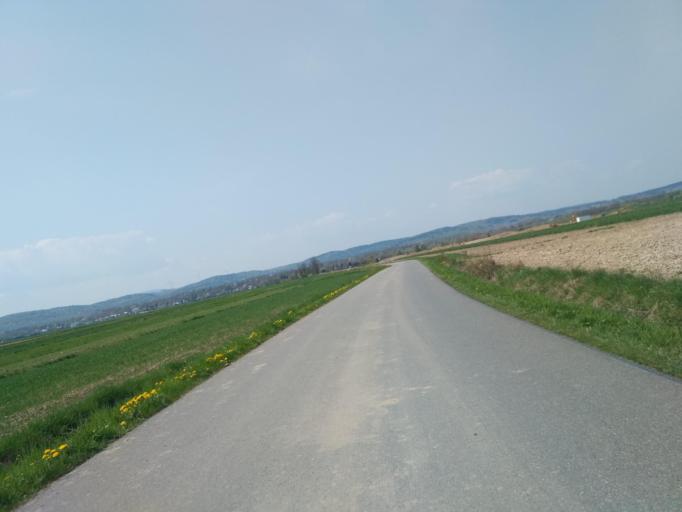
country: PL
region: Subcarpathian Voivodeship
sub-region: Krosno
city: Krosno
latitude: 49.6519
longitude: 21.7384
